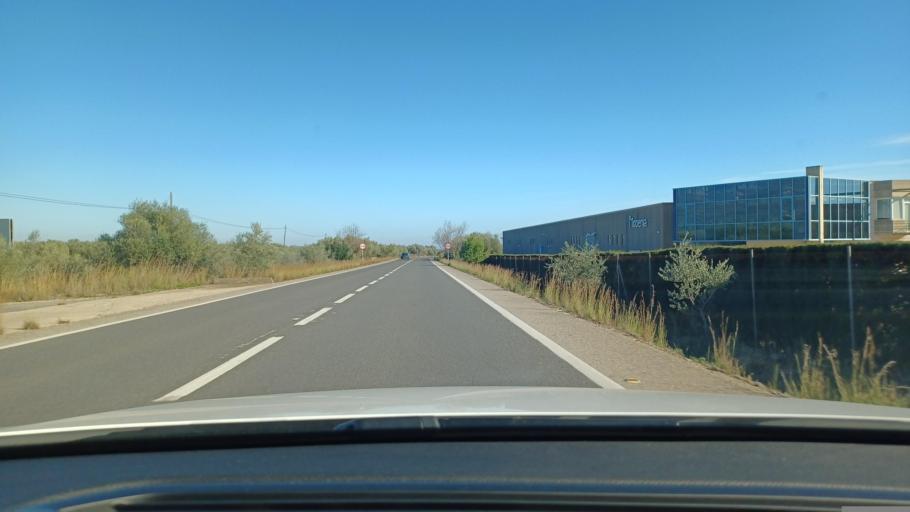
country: ES
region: Valencia
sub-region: Provincia de Castello
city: Rosell
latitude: 40.6364
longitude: 0.3214
